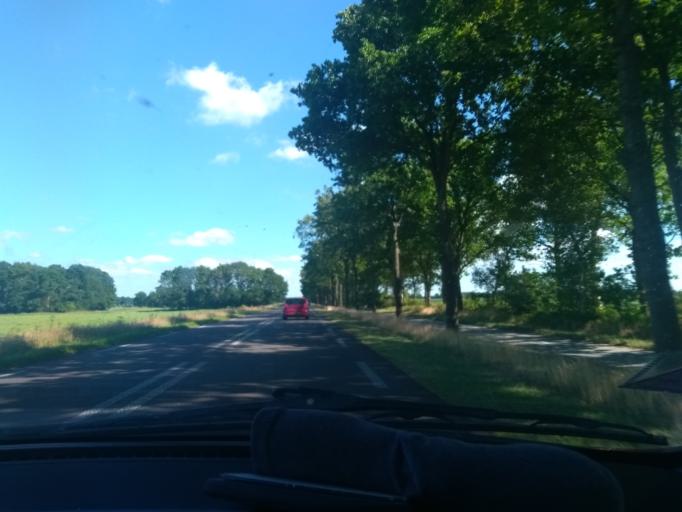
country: NL
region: Drenthe
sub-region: Gemeente Tynaarlo
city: Vries
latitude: 53.1171
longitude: 6.5113
